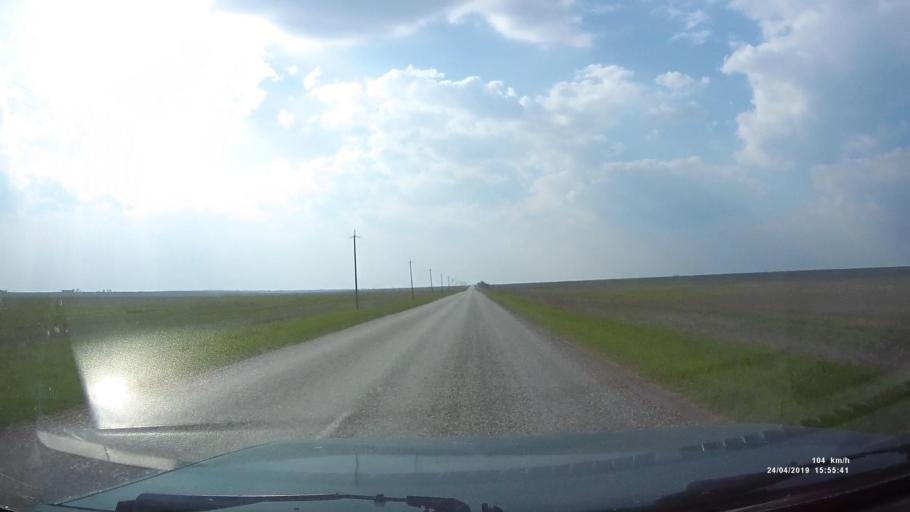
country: RU
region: Kalmykiya
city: Yashalta
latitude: 46.5922
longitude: 42.5442
